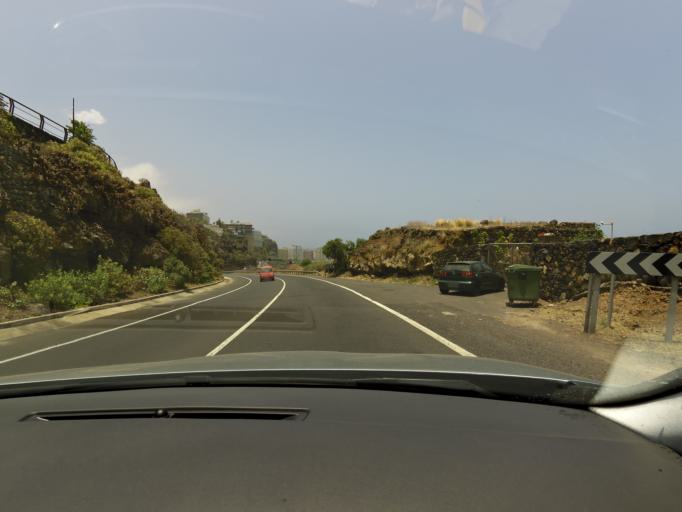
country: ES
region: Canary Islands
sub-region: Provincia de Santa Cruz de Tenerife
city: Puerto de la Cruz
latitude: 28.4171
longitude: -16.5300
